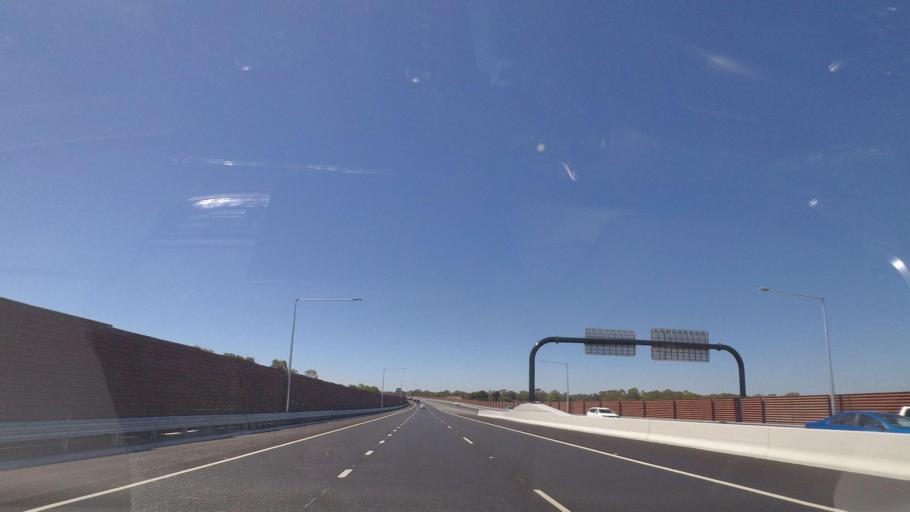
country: AU
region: Victoria
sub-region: Kingston
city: Waterways
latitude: -38.0048
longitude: 145.1227
